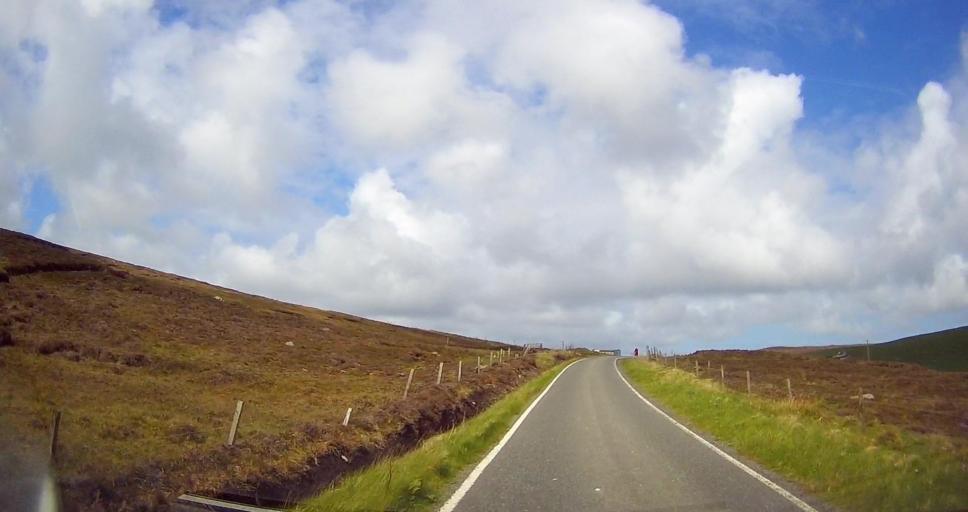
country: GB
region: Scotland
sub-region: Shetland Islands
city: Lerwick
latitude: 60.3003
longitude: -1.3407
